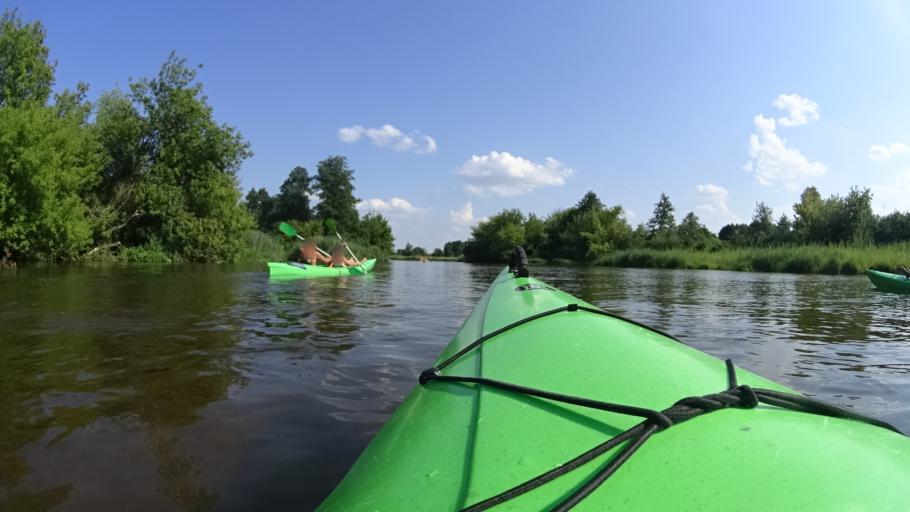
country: PL
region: Masovian Voivodeship
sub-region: Powiat bialobrzeski
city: Bialobrzegi
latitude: 51.6631
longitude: 20.9005
